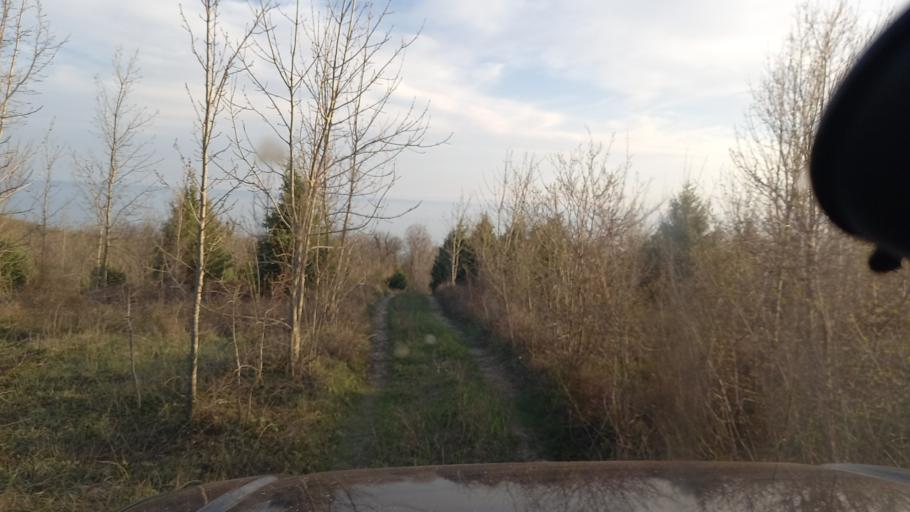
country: RU
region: Krasnodarskiy
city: Arkhipo-Osipovka
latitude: 44.3605
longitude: 38.5681
